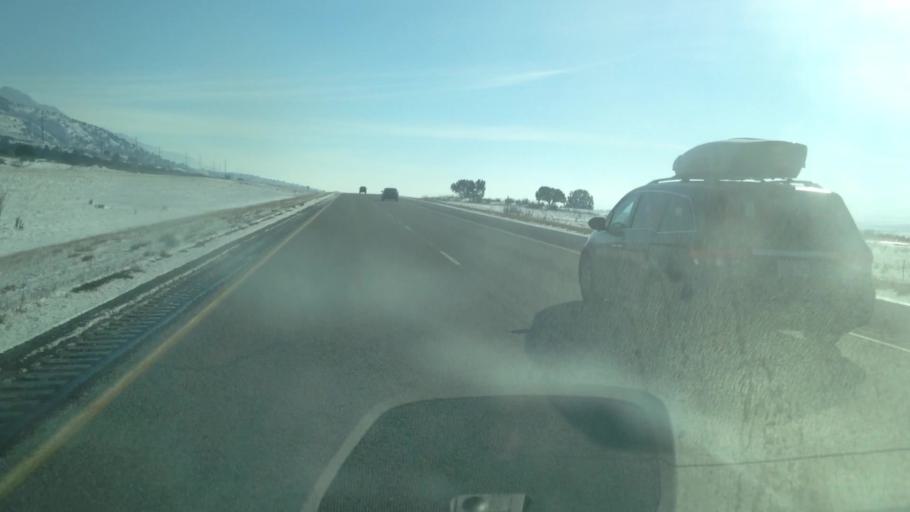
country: US
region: Idaho
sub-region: Oneida County
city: Malad City
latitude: 42.0127
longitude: -112.2029
